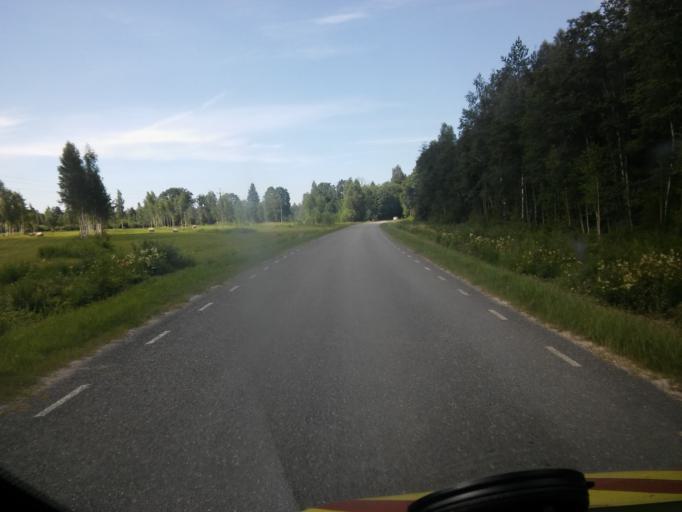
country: EE
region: Paernumaa
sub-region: Sindi linn
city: Sindi
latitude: 58.2511
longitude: 24.7613
